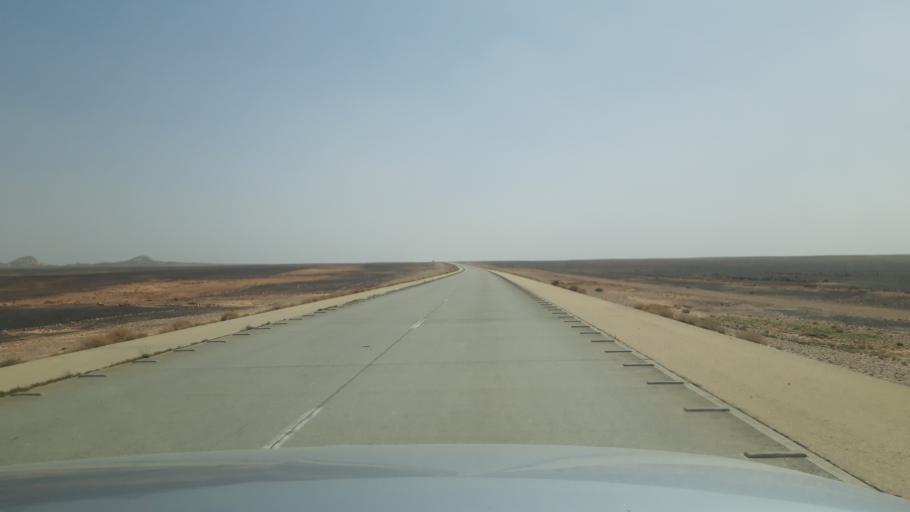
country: SA
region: Al Jawf
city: Al Qurayyat
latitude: 31.0171
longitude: 36.6338
